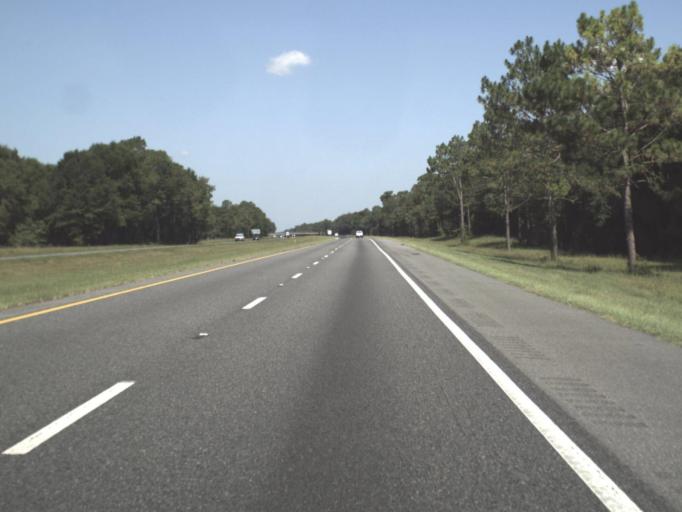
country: US
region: Florida
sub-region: Suwannee County
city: Live Oak
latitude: 30.3535
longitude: -83.1693
